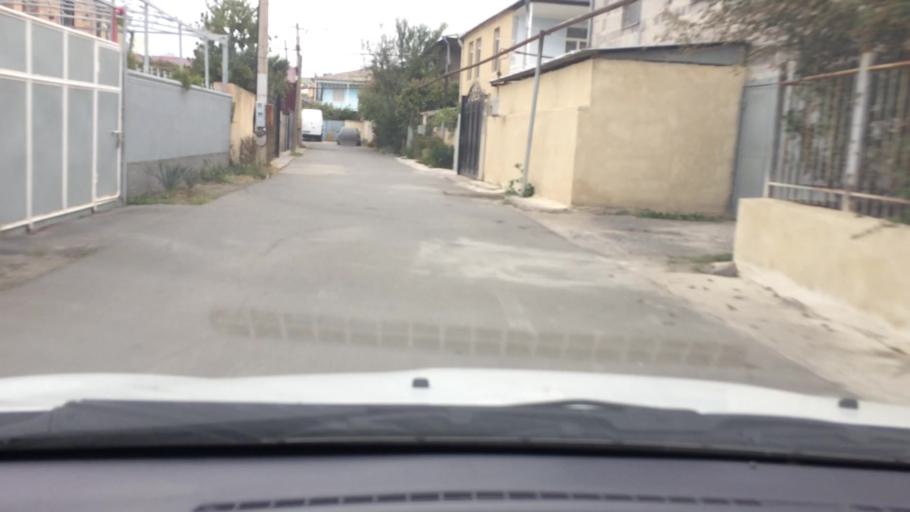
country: GE
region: Kvemo Kartli
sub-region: Marneuli
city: Marneuli
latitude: 41.4825
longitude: 44.7994
